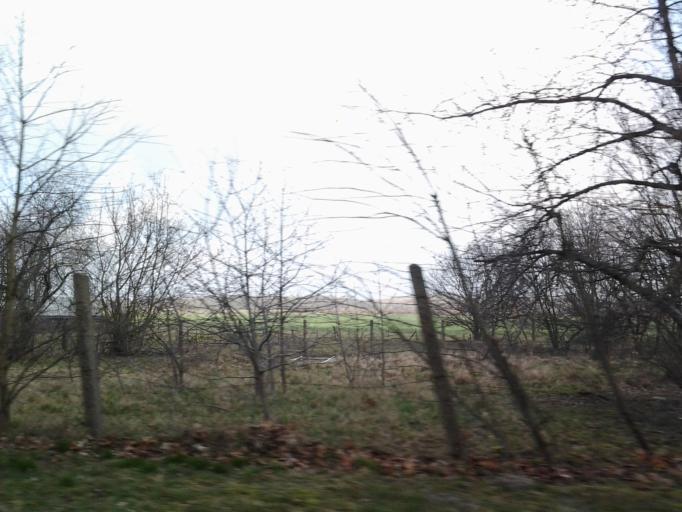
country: DE
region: Berlin
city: Staaken
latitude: 52.5071
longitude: 13.1479
